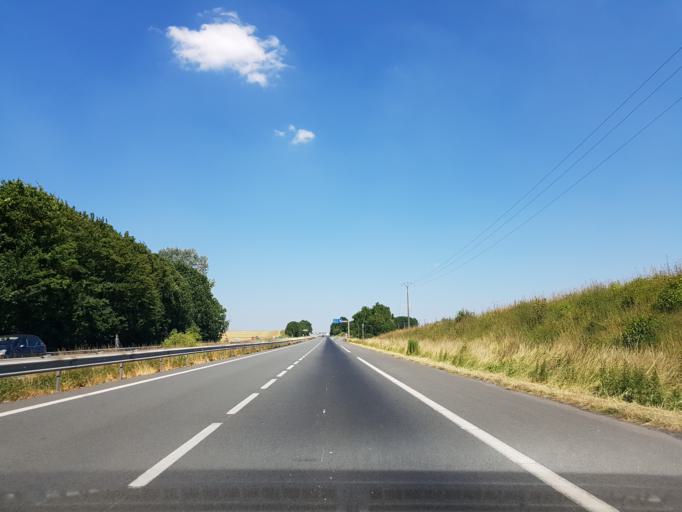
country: FR
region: Nord-Pas-de-Calais
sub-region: Departement du Nord
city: Marcoing
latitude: 50.0849
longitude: 3.1727
